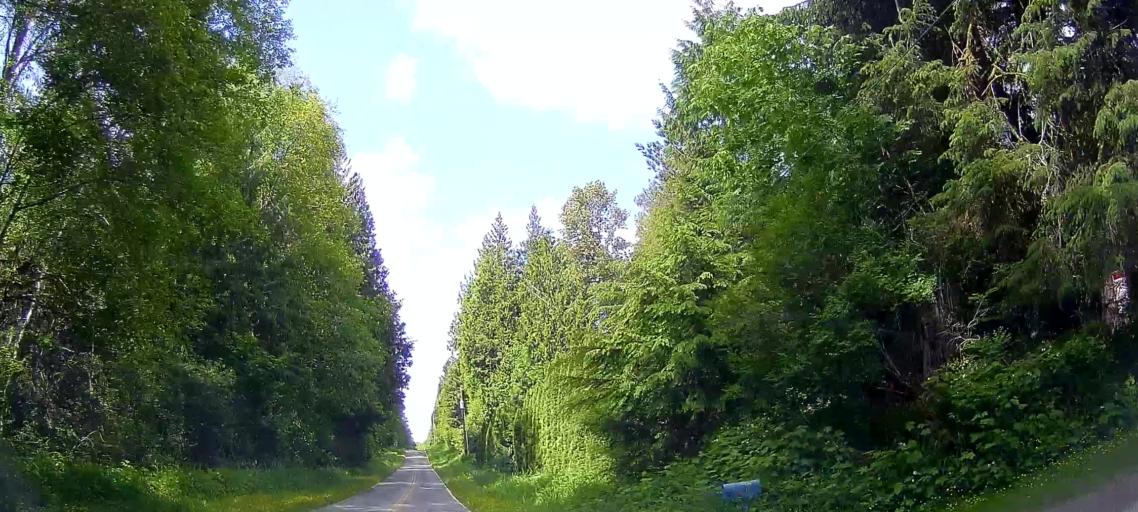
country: US
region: Washington
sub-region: Whatcom County
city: Sudden Valley
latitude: 48.6649
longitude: -122.1956
